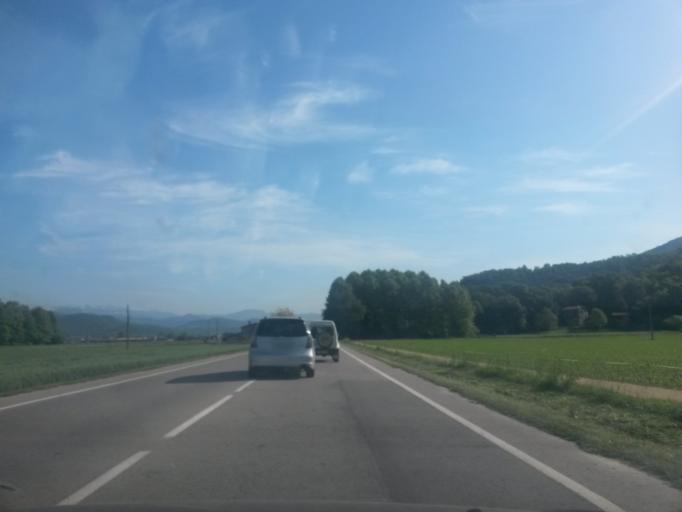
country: ES
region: Catalonia
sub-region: Provincia de Girona
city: Bas
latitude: 42.1326
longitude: 2.4520
